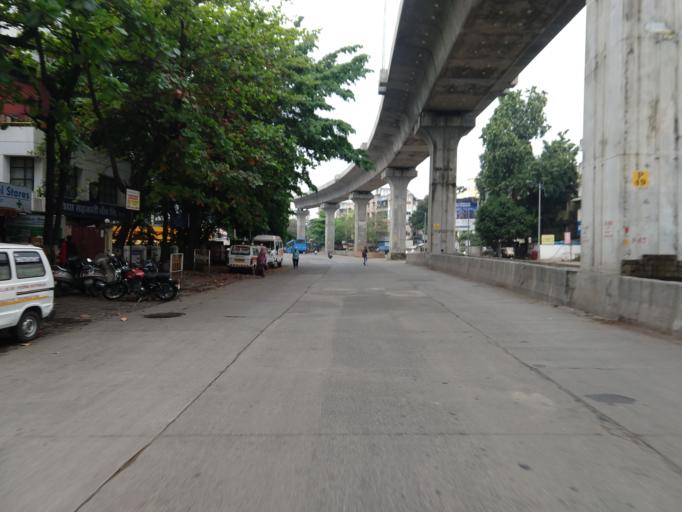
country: IN
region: Maharashtra
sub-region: Pune Division
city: Pune
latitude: 18.5094
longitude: 73.8128
